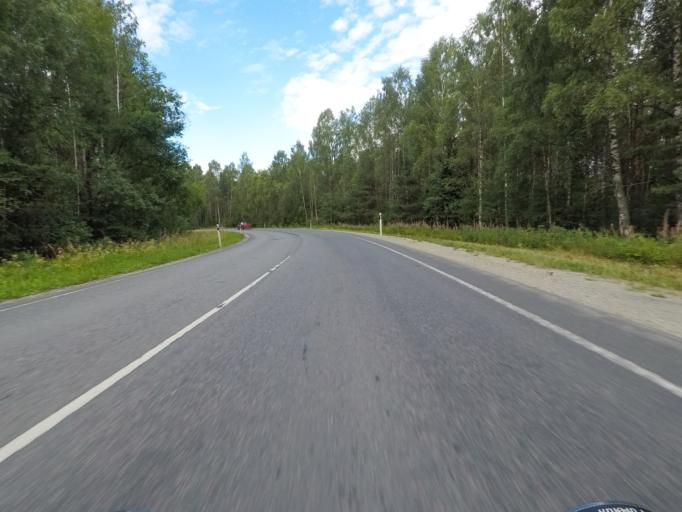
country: EE
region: Harju
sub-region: Saku vald
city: Saku
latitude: 59.3175
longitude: 24.6782
